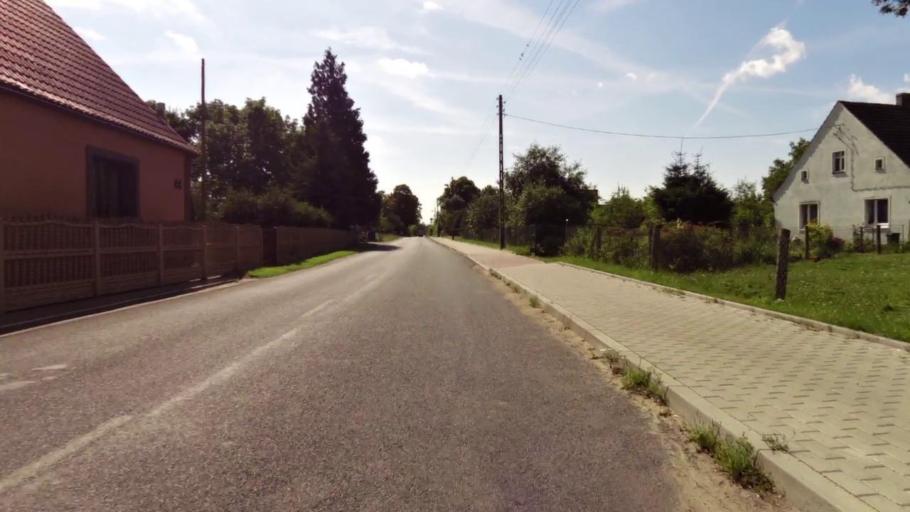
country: PL
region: West Pomeranian Voivodeship
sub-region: Powiat stargardzki
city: Dobrzany
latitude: 53.4080
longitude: 15.4285
